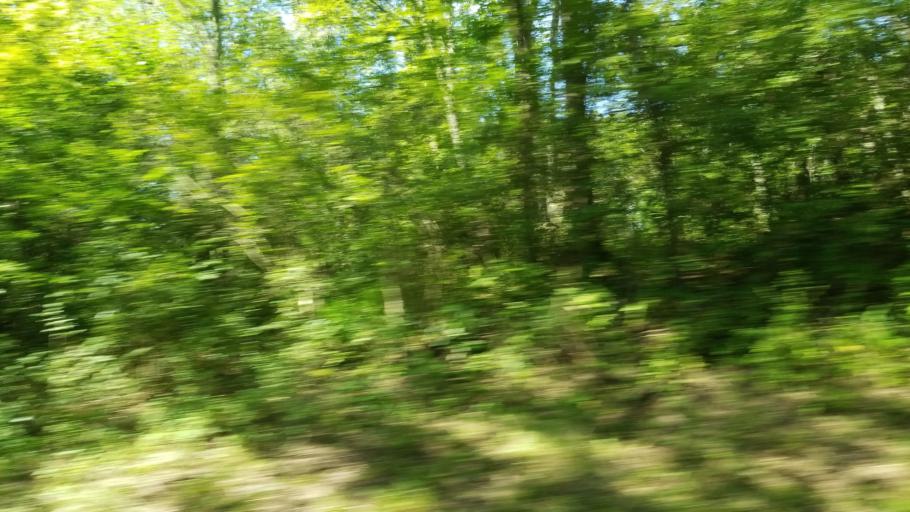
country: US
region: Illinois
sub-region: Saline County
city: Carrier Mills
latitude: 37.7990
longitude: -88.7384
